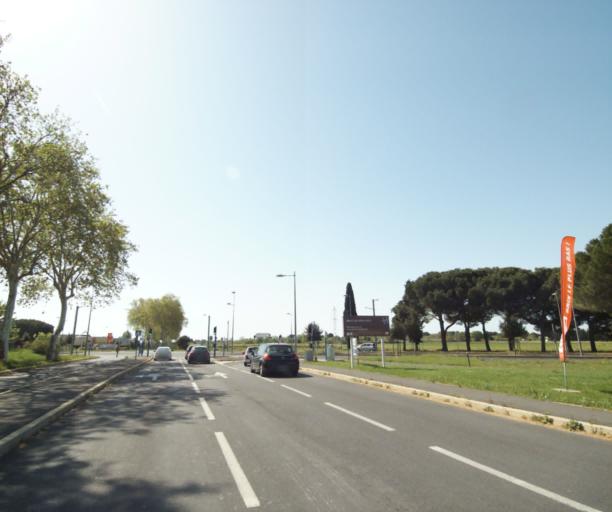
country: FR
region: Languedoc-Roussillon
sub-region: Departement de l'Herault
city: Perols
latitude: 43.5803
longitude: 3.9318
